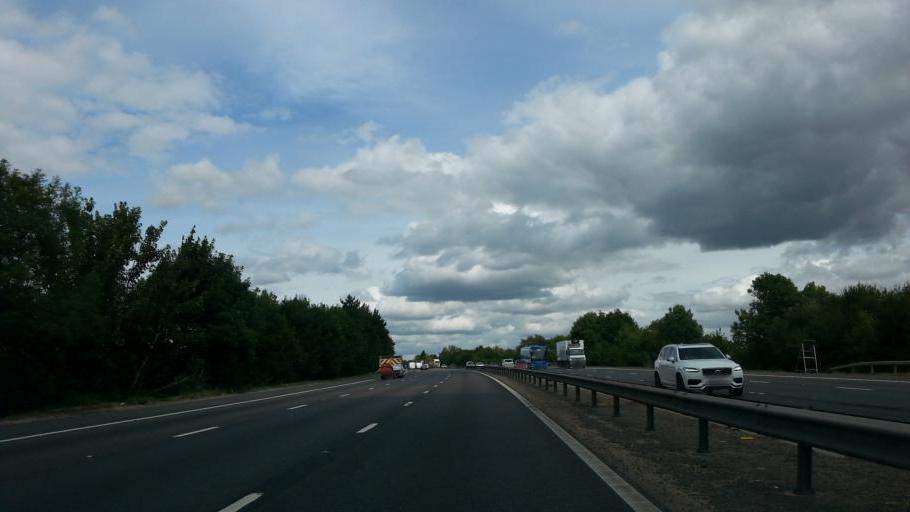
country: GB
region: England
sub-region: Essex
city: Little Hallingbury
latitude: 51.8124
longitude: 0.1810
